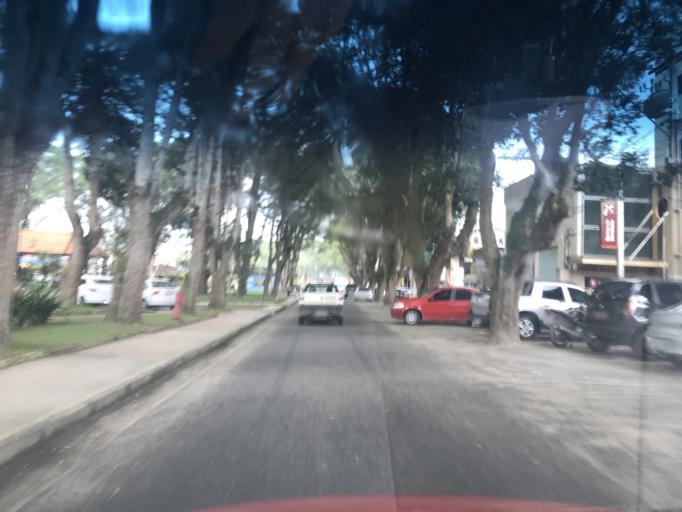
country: BR
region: Bahia
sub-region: Cruz Das Almas
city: Cruz das Almas
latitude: -12.6728
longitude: -39.1012
